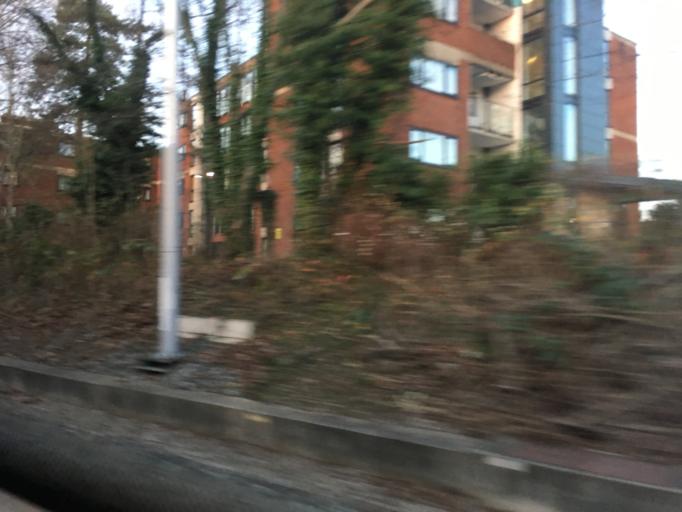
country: GB
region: England
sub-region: Manchester
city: Chorlton cum Hardy
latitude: 53.4415
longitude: -2.2718
